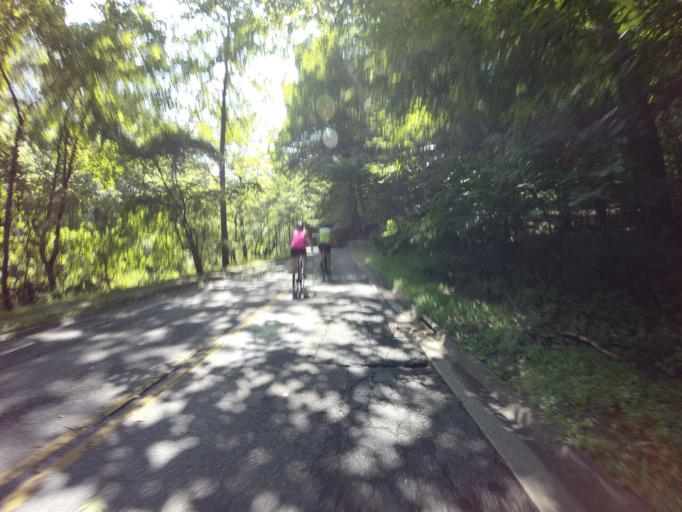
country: US
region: Maryland
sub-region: Montgomery County
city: Silver Spring
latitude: 38.9845
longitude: -77.0469
